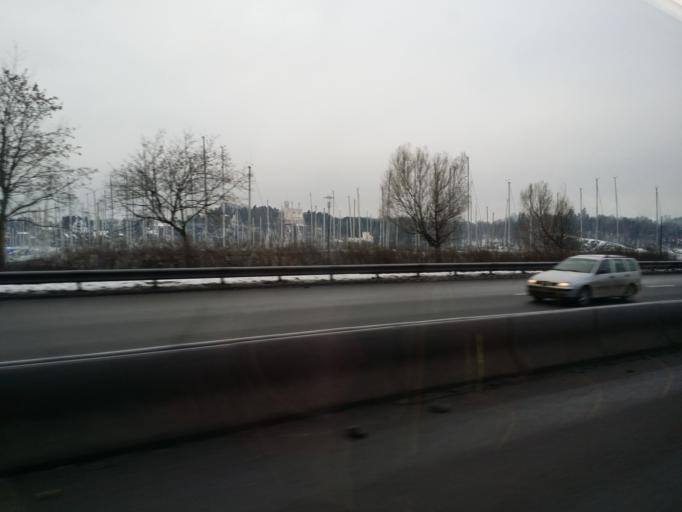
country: NO
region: Oslo
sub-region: Oslo
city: Sjolyststranda
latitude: 59.9116
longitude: 10.7034
